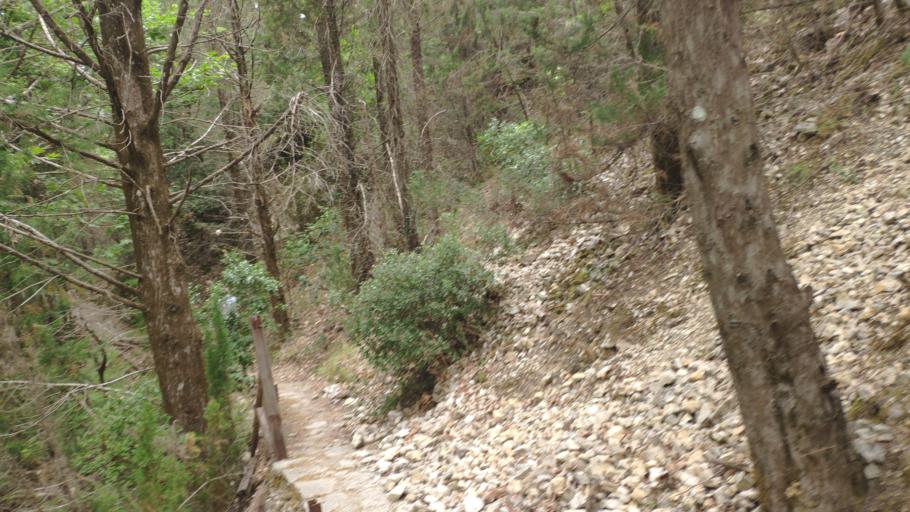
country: GR
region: Ionian Islands
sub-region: Lefkada
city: Lefkada
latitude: 38.8005
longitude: 20.6702
